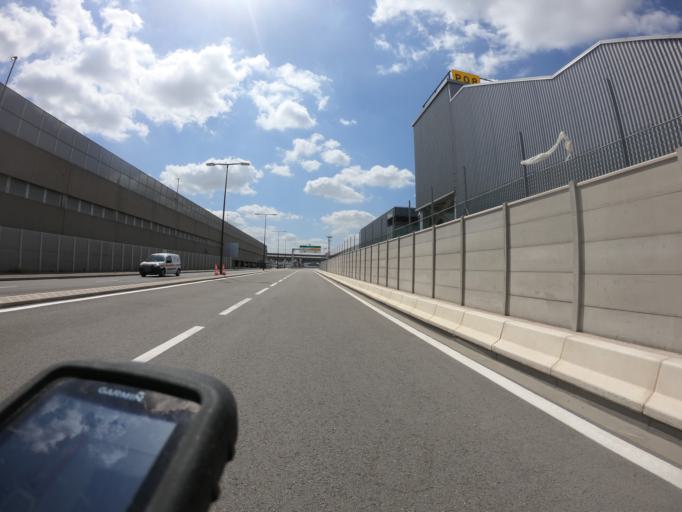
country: FR
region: Ile-de-France
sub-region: Departement du Val-de-Marne
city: Rungis
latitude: 48.7317
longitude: 2.3622
